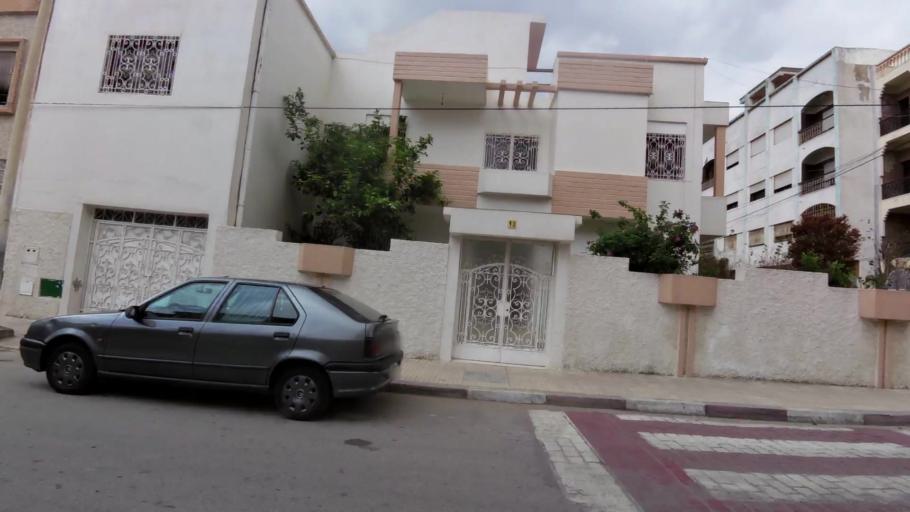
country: MA
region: Tanger-Tetouan
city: Tetouan
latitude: 35.5655
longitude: -5.3604
